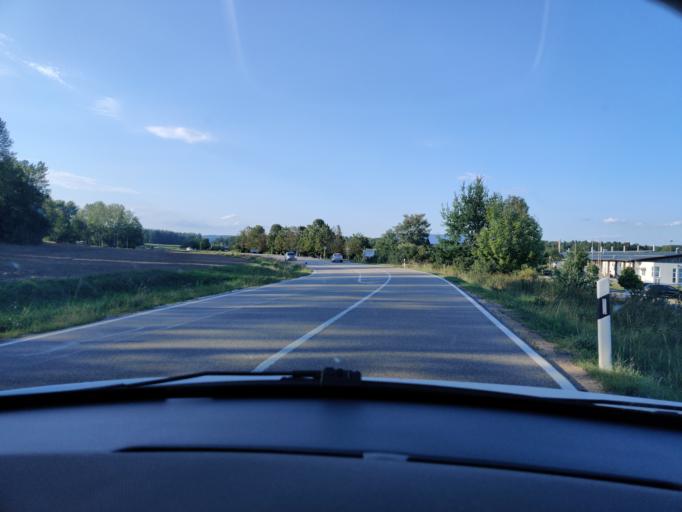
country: DE
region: Bavaria
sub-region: Upper Palatinate
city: Schwarzenfeld
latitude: 49.3980
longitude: 12.1345
